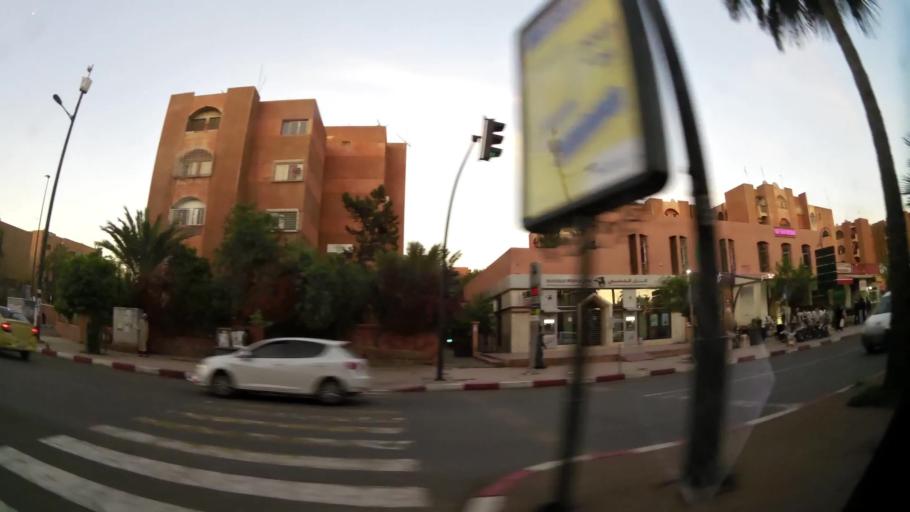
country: MA
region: Marrakech-Tensift-Al Haouz
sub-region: Marrakech
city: Marrakesh
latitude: 31.6439
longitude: -8.0006
